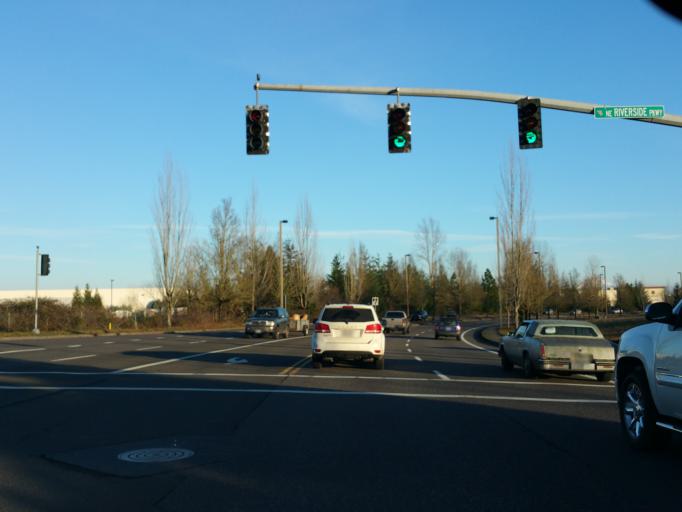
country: US
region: Oregon
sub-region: Multnomah County
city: Fairview
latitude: 45.5532
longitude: -122.4810
